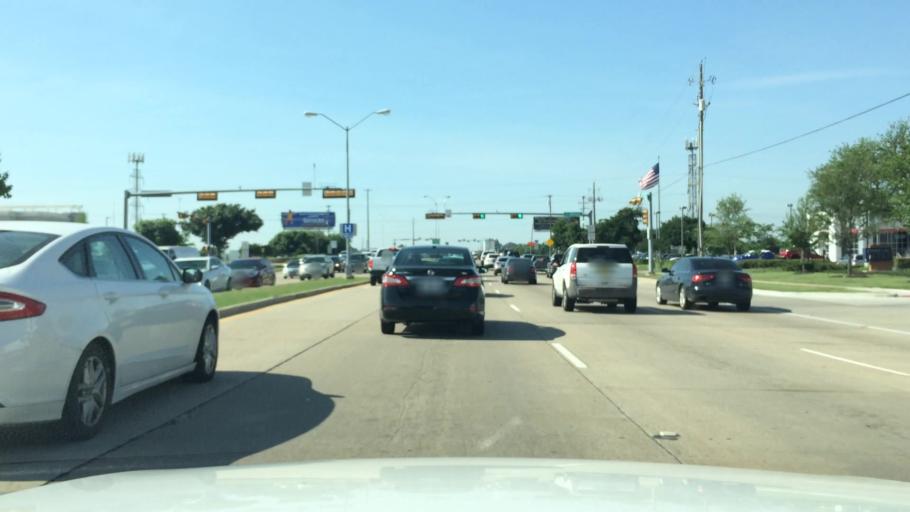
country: US
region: Texas
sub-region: Dallas County
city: Addison
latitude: 33.0153
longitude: -96.7954
